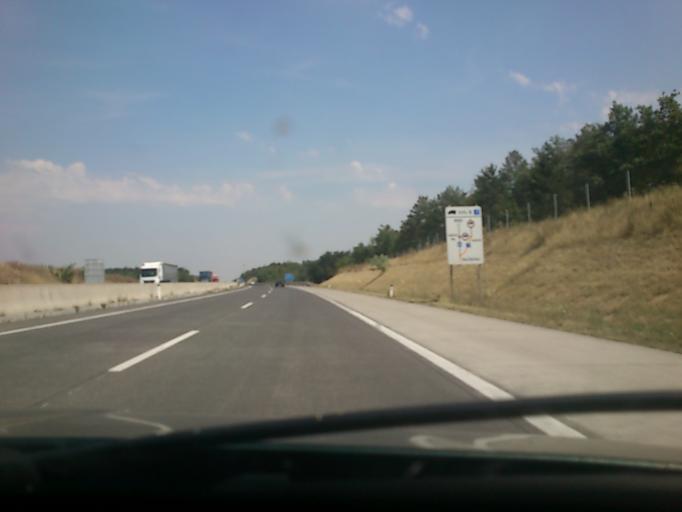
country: AT
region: Lower Austria
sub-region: Politischer Bezirk Mistelbach
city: Wolkersdorf im Weinviertel
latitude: 48.4072
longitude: 16.5351
